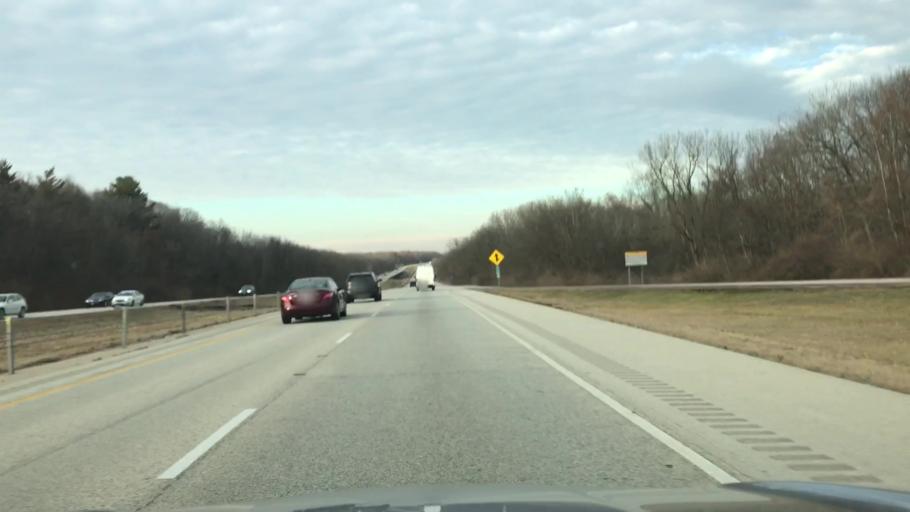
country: US
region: Illinois
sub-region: Sangamon County
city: Sherman
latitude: 39.8654
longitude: -89.5956
